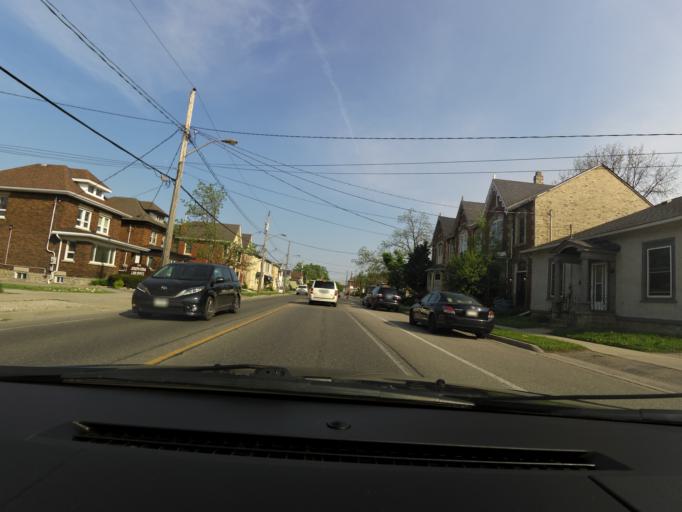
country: CA
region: Ontario
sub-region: Wellington County
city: Guelph
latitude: 43.5512
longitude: -80.2583
